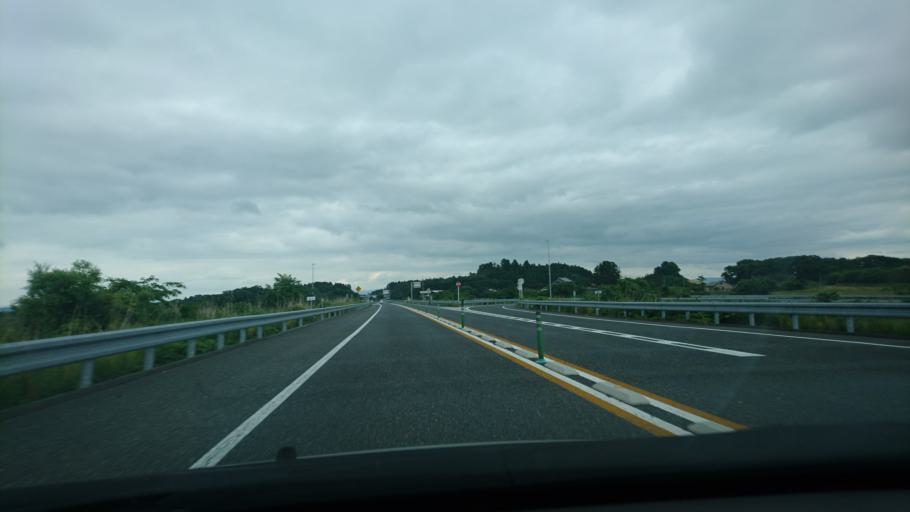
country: JP
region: Miyagi
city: Kogota
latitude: 38.7305
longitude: 141.0832
